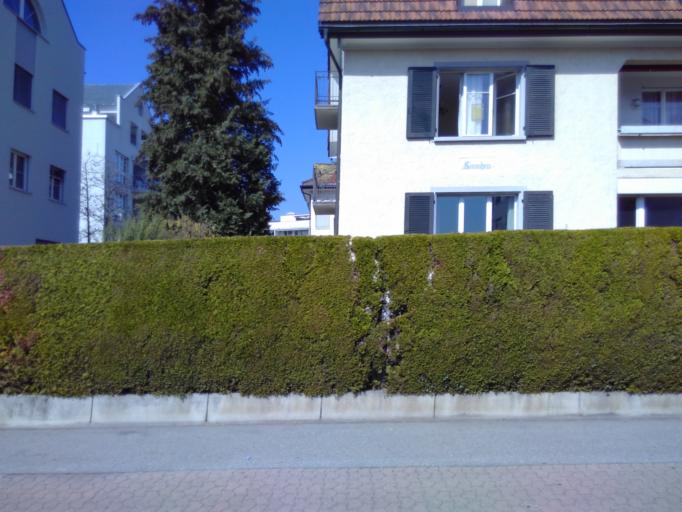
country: CH
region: Saint Gallen
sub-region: Wahlkreis See-Gaster
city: Rapperswil
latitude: 47.2285
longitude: 8.8288
